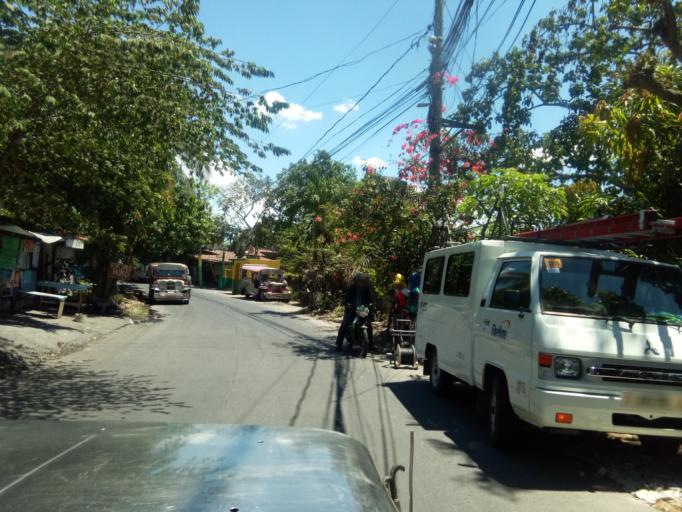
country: PH
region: Calabarzon
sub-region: Province of Cavite
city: Dasmarinas
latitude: 14.3233
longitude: 120.9667
